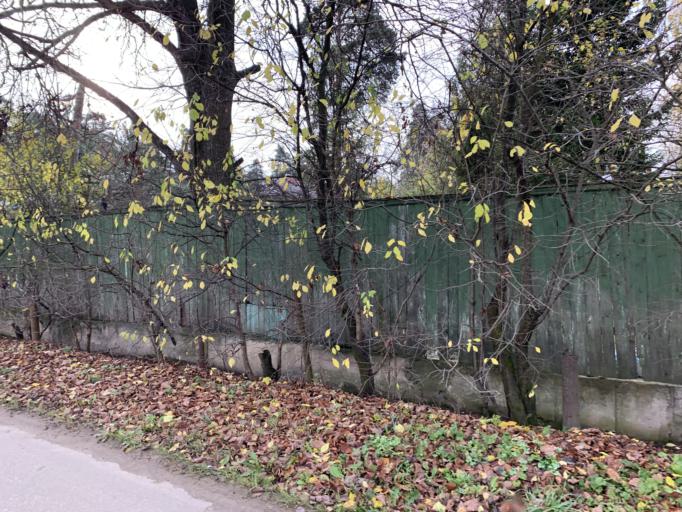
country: RU
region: Moskovskaya
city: Mamontovka
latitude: 55.9871
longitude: 37.8447
